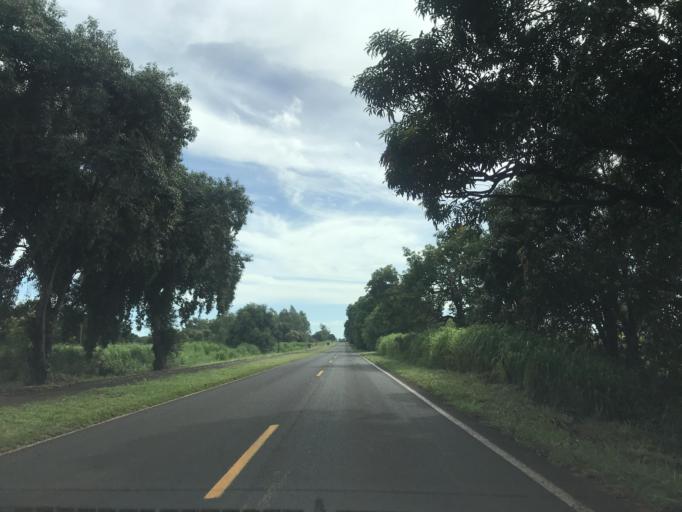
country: BR
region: Parana
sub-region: Terra Rica
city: Terra Rica
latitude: -22.7590
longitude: -52.6327
